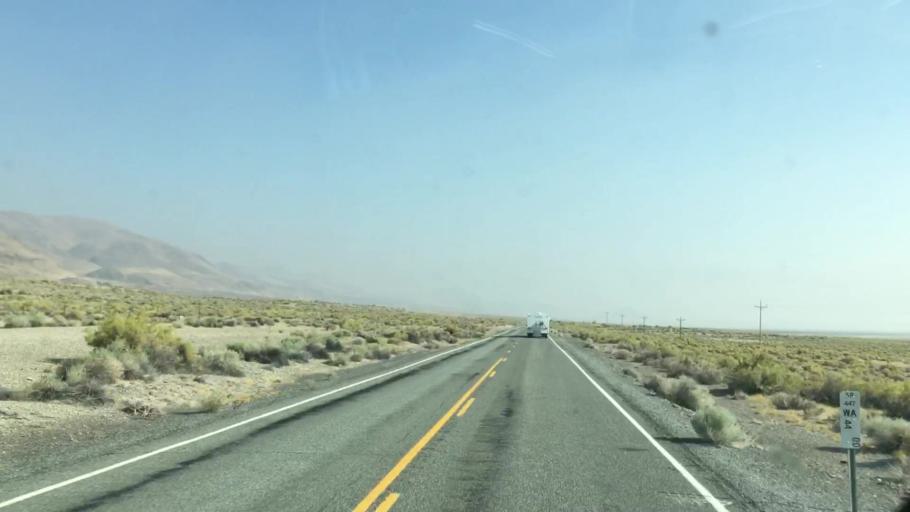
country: US
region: Nevada
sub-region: Lyon County
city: Fernley
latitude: 40.2187
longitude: -119.3691
